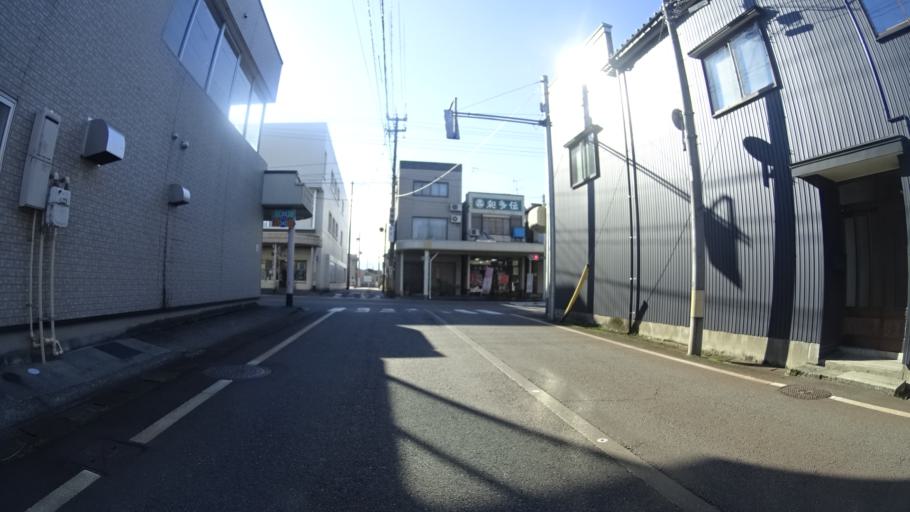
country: JP
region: Niigata
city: Mitsuke
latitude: 37.5273
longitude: 138.9229
